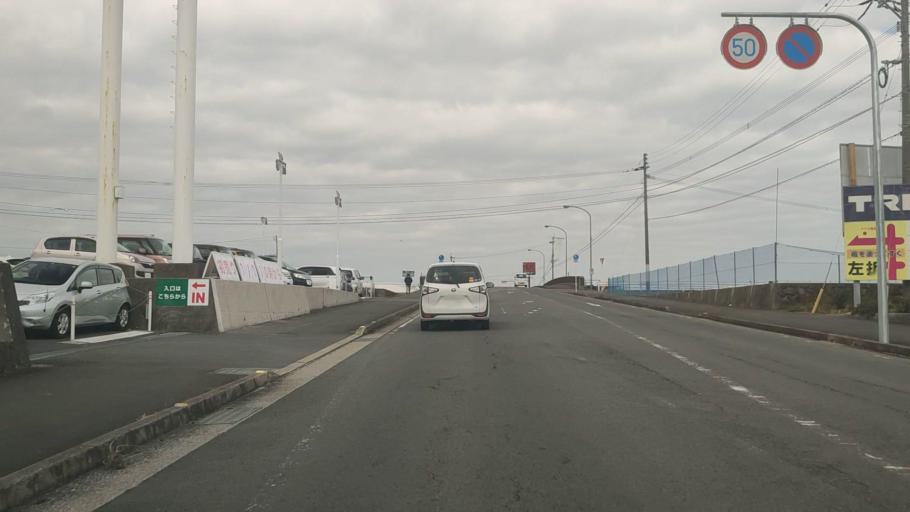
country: JP
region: Nagasaki
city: Shimabara
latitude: 32.8070
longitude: 130.3613
